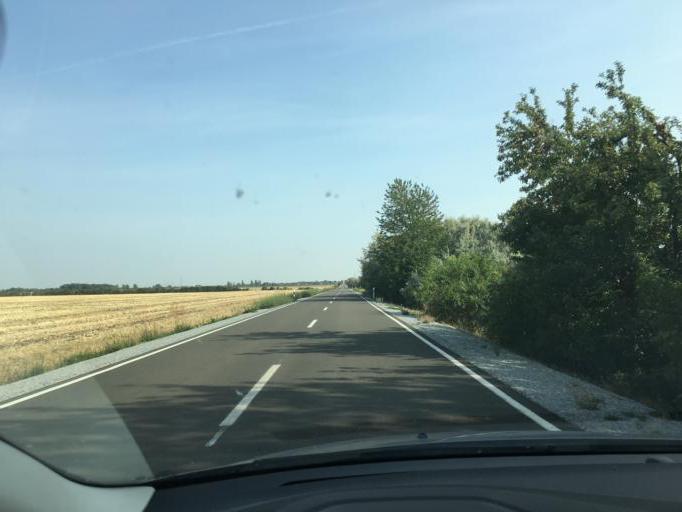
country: DE
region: Saxony-Anhalt
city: Baalberge
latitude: 51.8009
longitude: 11.8559
